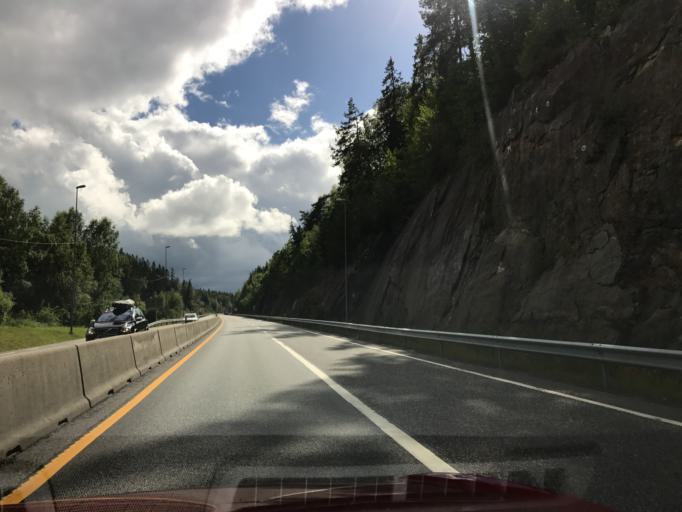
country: NO
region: Aust-Agder
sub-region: Gjerstad
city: Gjerstad
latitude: 58.8329
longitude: 9.0880
